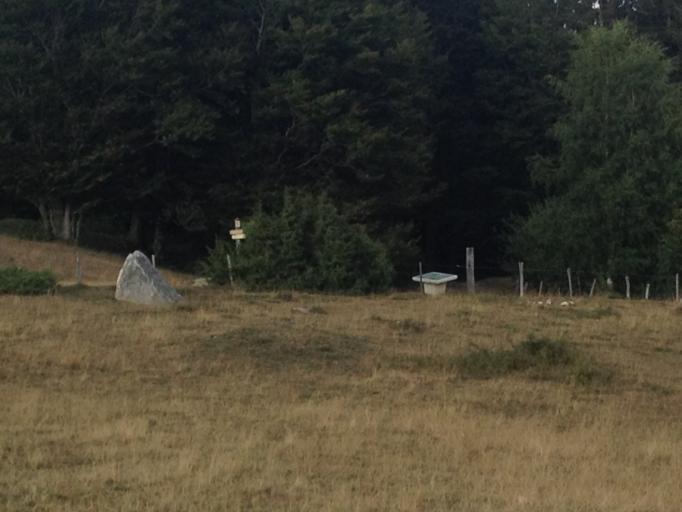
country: FR
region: Rhone-Alpes
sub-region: Departement de la Haute-Savoie
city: Collonges-sous-Saleve
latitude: 46.1356
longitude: 6.1825
